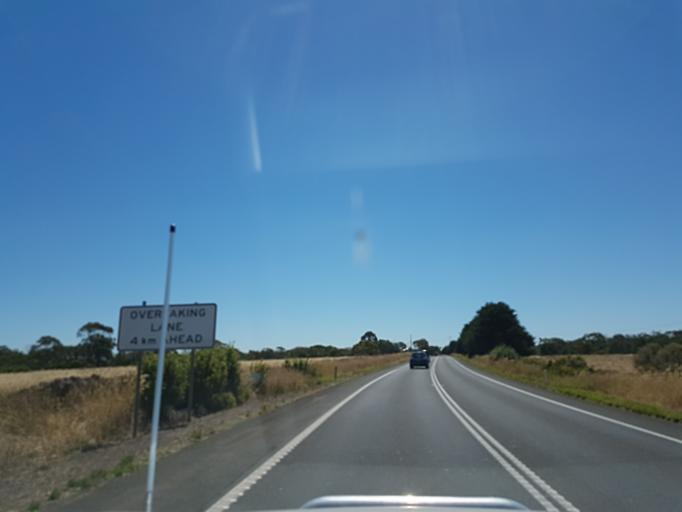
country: AU
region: Victoria
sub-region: Colac-Otway
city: Colac
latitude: -38.3394
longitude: 143.3610
